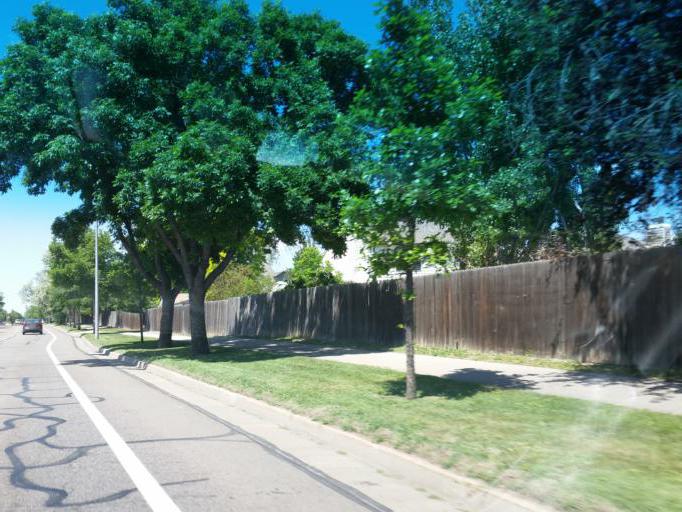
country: US
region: Colorado
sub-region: Larimer County
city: Fort Collins
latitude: 40.5269
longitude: -105.0961
